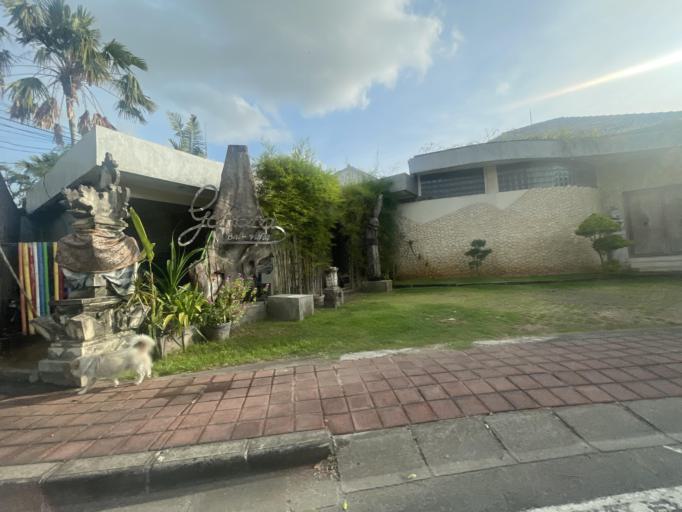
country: ID
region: Bali
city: Kuta
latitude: -8.6907
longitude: 115.1752
